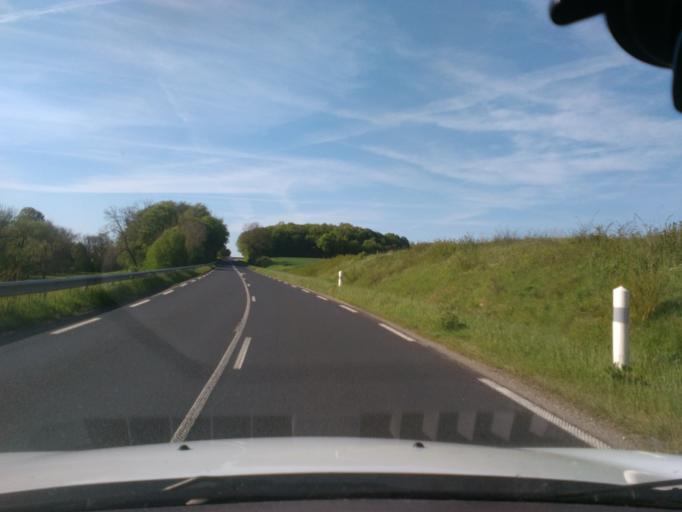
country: FR
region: Lorraine
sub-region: Departement des Vosges
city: Mirecourt
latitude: 48.3407
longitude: 6.1396
